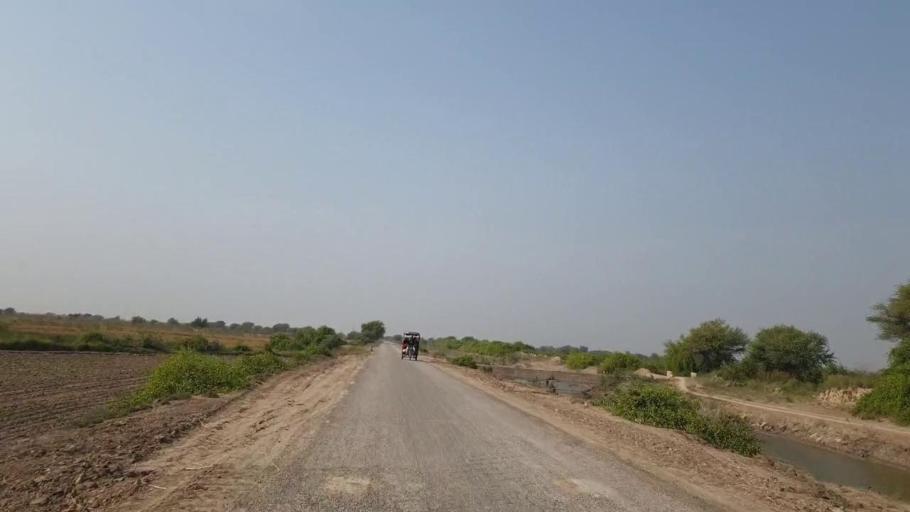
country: PK
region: Sindh
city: Matli
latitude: 24.9571
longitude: 68.5244
